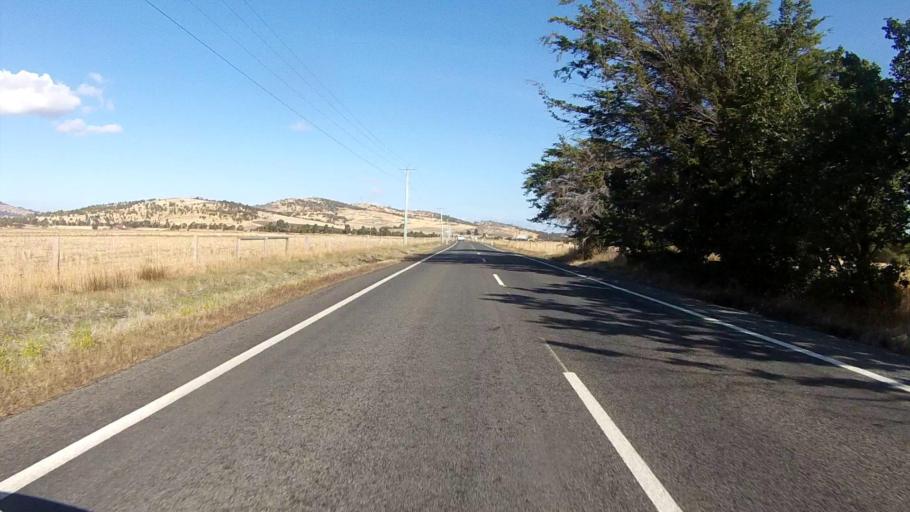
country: AU
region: Tasmania
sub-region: Sorell
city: Sorell
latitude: -42.7442
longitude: 147.5348
